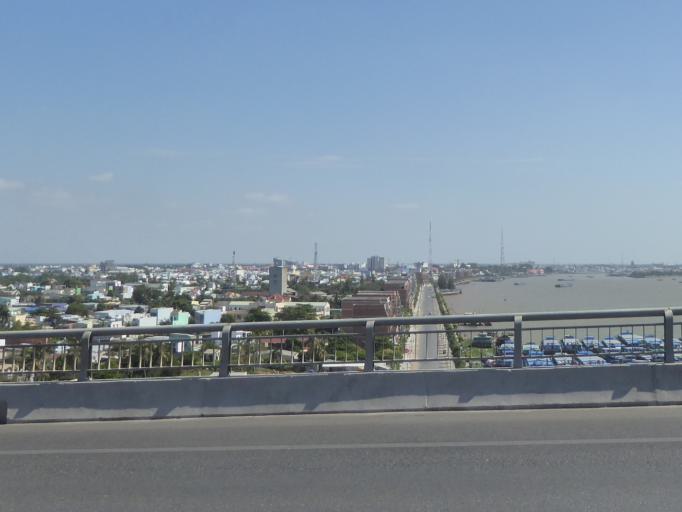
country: VN
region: Tien Giang
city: My Tho
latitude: 10.3466
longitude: 106.3417
